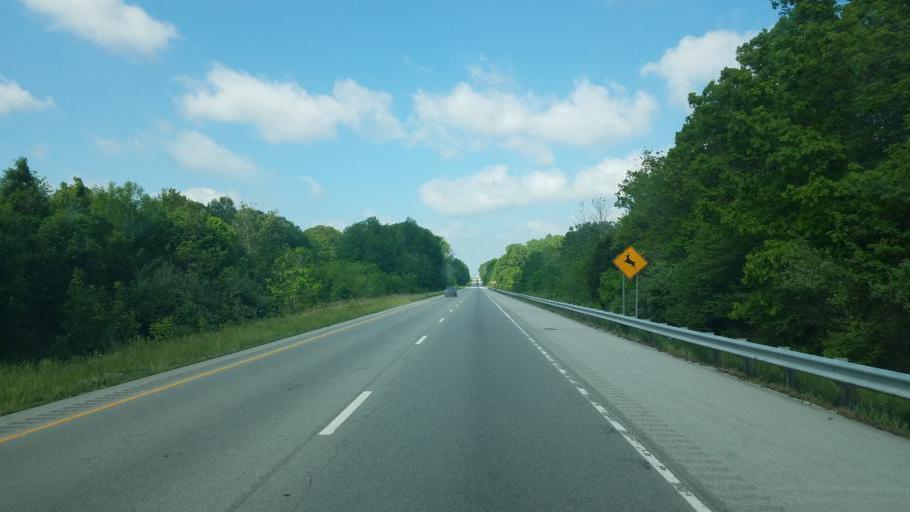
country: US
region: Indiana
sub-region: Putnam County
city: Cloverdale
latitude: 39.5416
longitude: -86.7488
